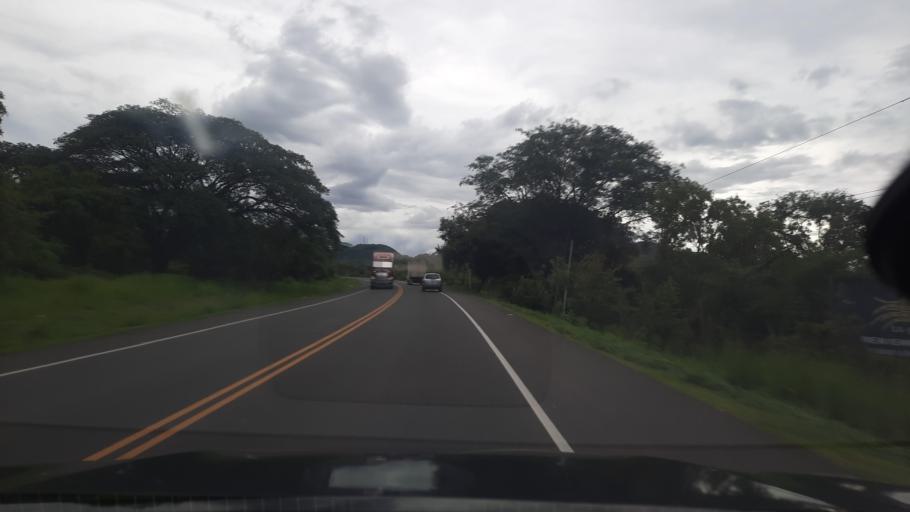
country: HN
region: Choluteca
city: Marcovia
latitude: 13.3743
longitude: -87.3008
